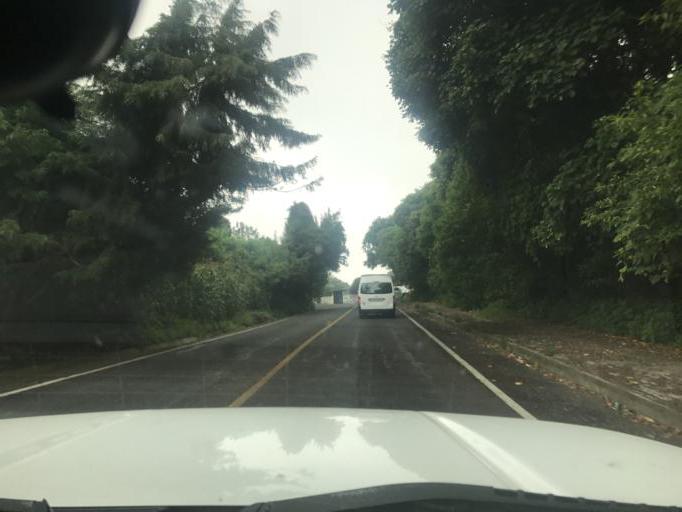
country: MX
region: Morelos
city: Ocuituco
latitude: 18.8828
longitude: -98.7648
